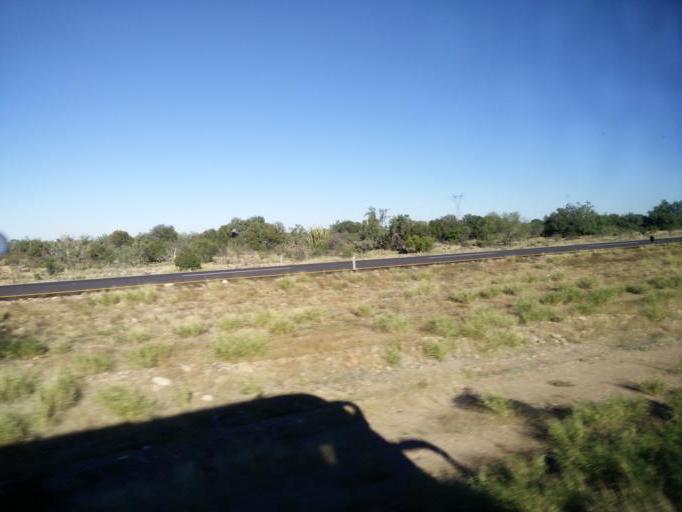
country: MX
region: Sonora
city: Hermosillo
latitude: 28.6467
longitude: -111.0062
